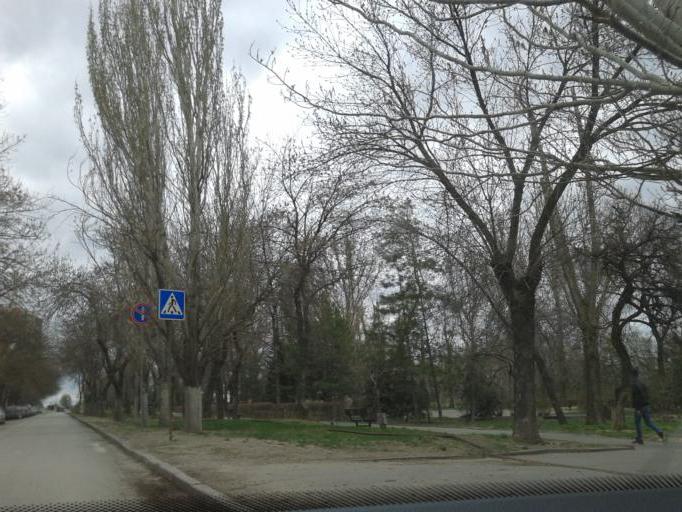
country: RU
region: Volgograd
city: Volgograd
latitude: 48.7126
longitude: 44.5312
